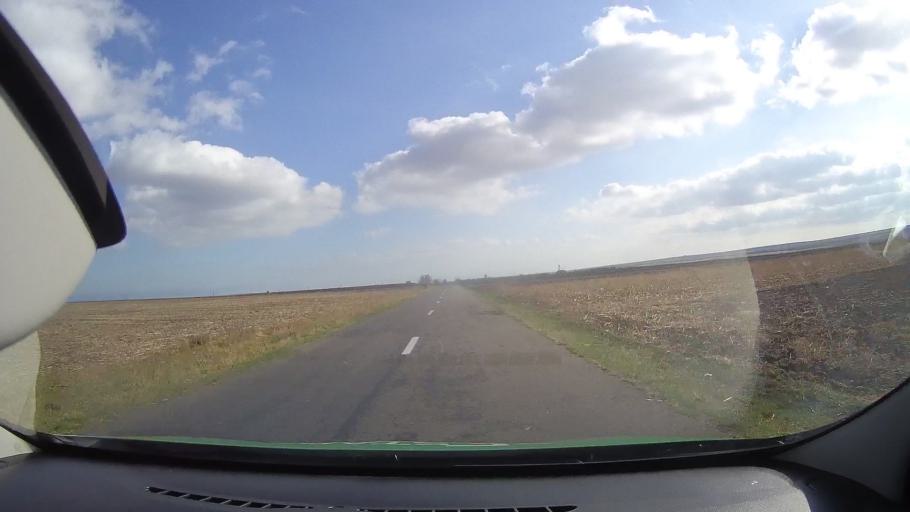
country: RO
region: Constanta
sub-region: Comuna Cogealac
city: Tariverde
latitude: 44.5552
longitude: 28.6187
